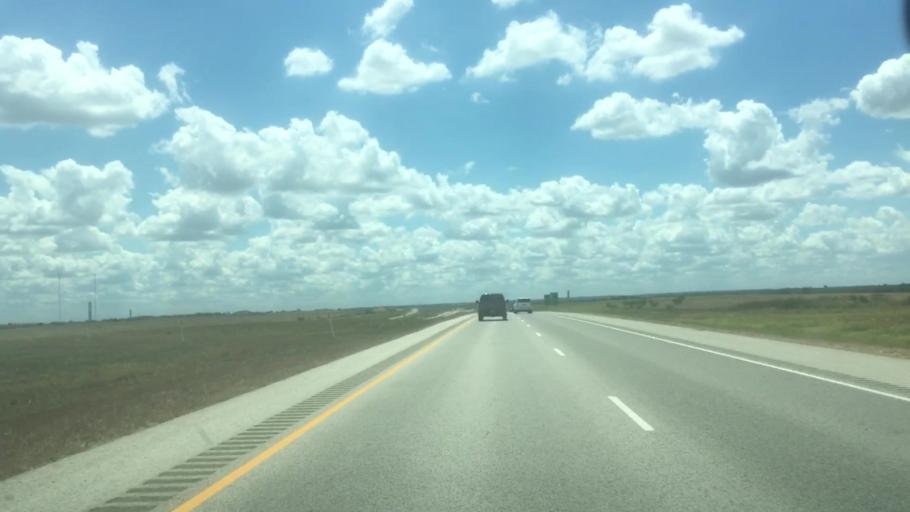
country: US
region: Texas
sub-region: Caldwell County
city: Martindale
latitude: 29.7984
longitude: -97.7798
